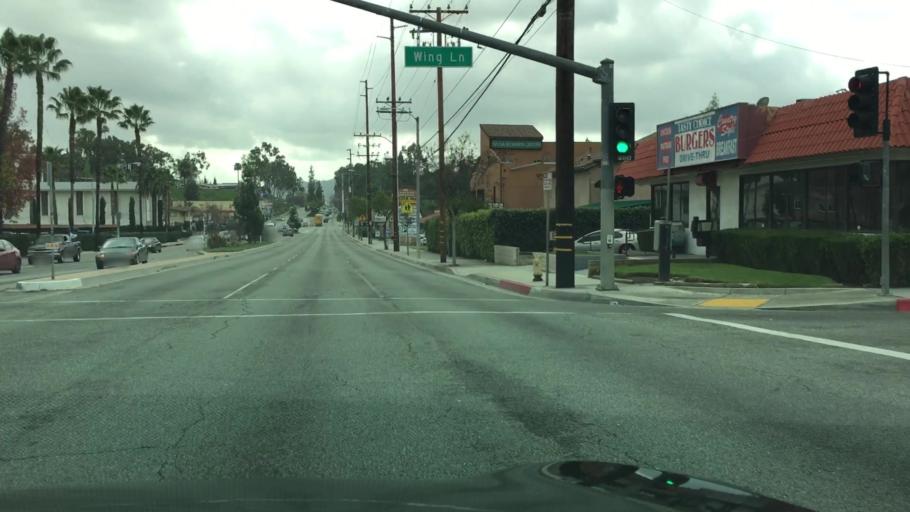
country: US
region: California
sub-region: Los Angeles County
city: South San Jose Hills
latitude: 34.0274
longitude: -117.9167
